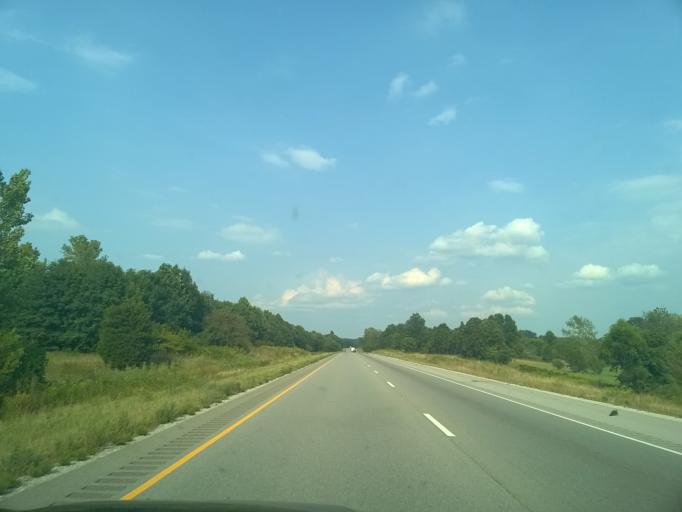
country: US
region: Indiana
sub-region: Vigo County
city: Seelyville
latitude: 39.4368
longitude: -87.2853
